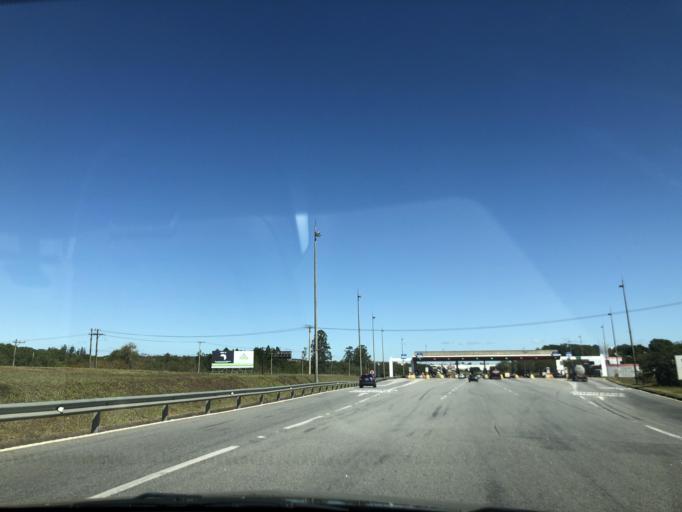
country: BR
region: Sao Paulo
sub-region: Sorocaba
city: Sorocaba
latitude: -23.4098
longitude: -47.3405
